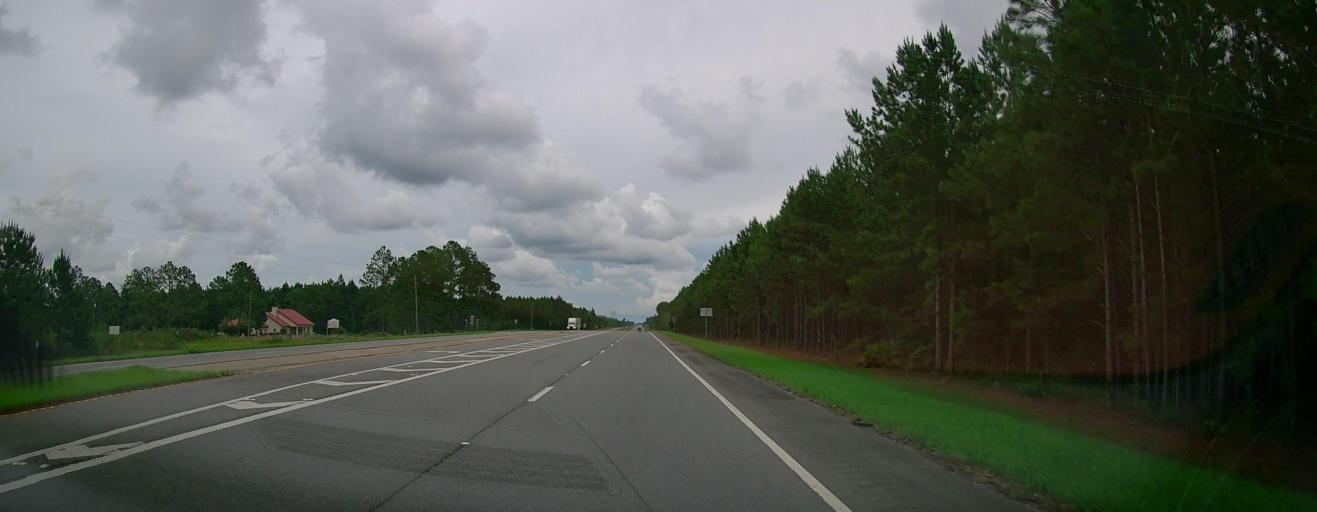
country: US
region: Georgia
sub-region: Wayne County
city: Jesup
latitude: 31.6835
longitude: -82.1011
